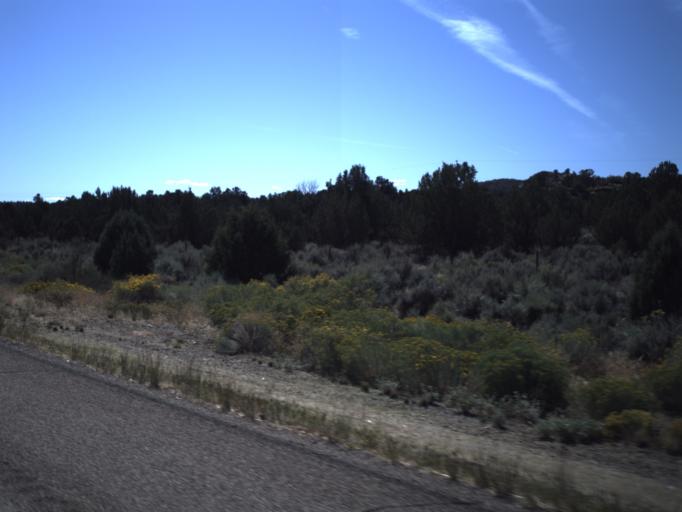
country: US
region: Utah
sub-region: Washington County
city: Ivins
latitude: 37.2667
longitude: -113.6381
